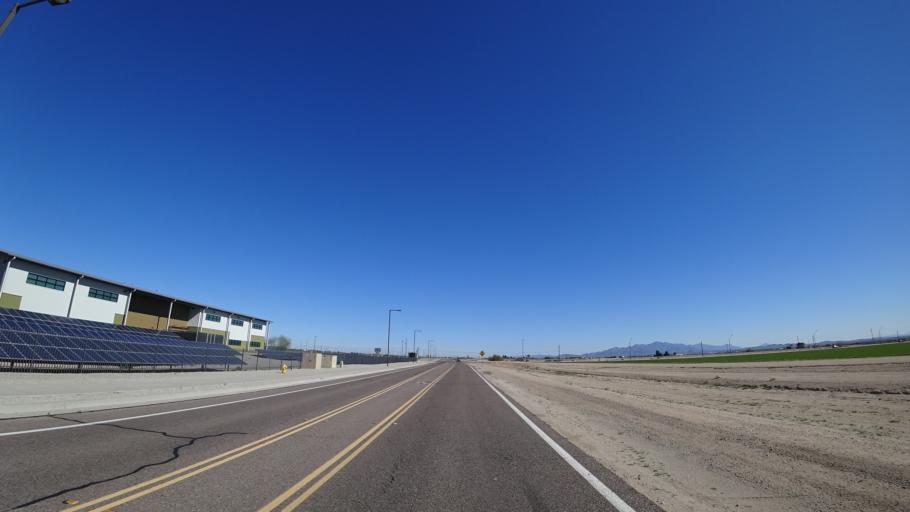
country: US
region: Arizona
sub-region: Maricopa County
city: Buckeye
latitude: 33.4174
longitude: -112.5759
